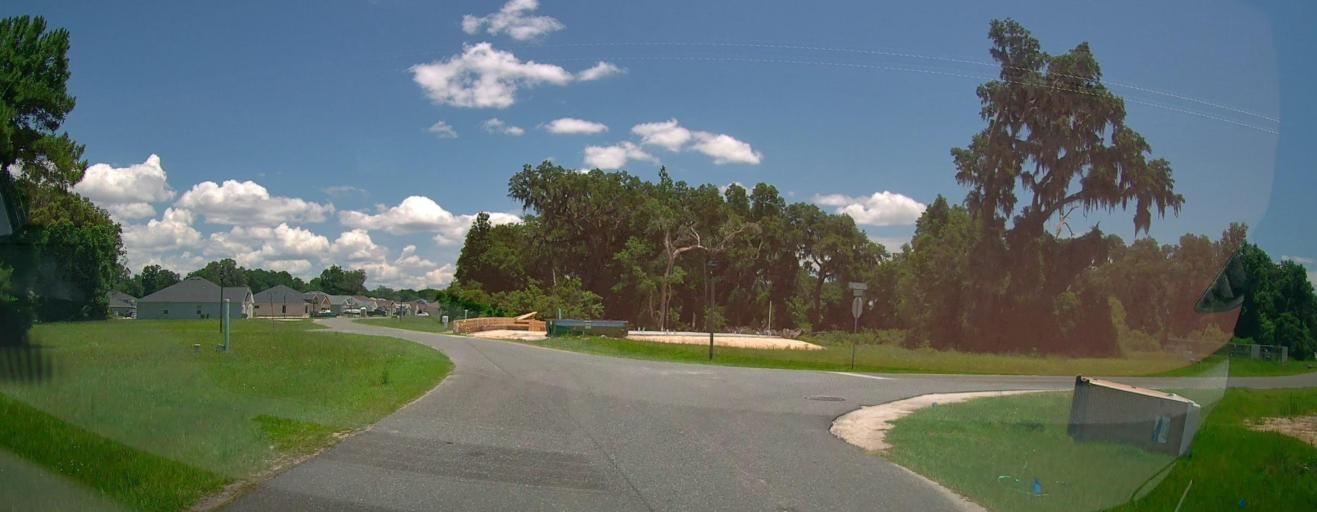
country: US
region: Florida
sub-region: Marion County
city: Belleview
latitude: 29.0908
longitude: -82.0704
